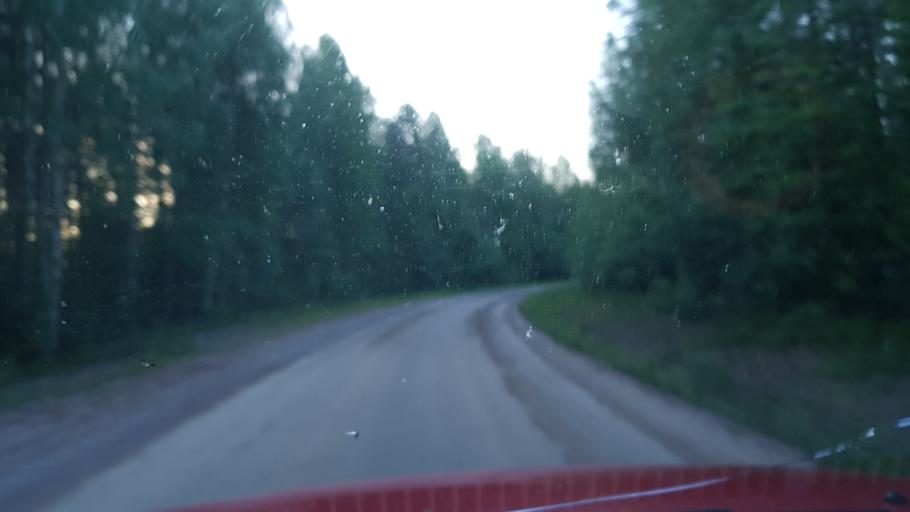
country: SE
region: Norrbotten
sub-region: Alvsbyns Kommun
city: AElvsbyn
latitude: 65.6971
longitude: 20.6696
